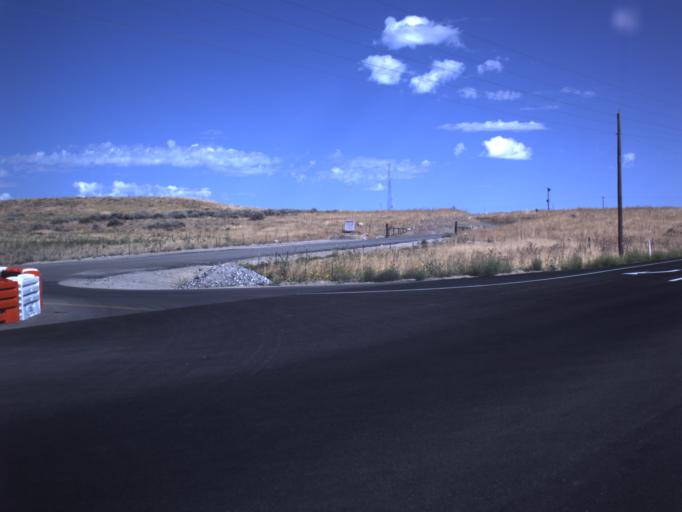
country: US
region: Utah
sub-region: Salt Lake County
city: Oquirrh
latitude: 40.6209
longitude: -112.0534
